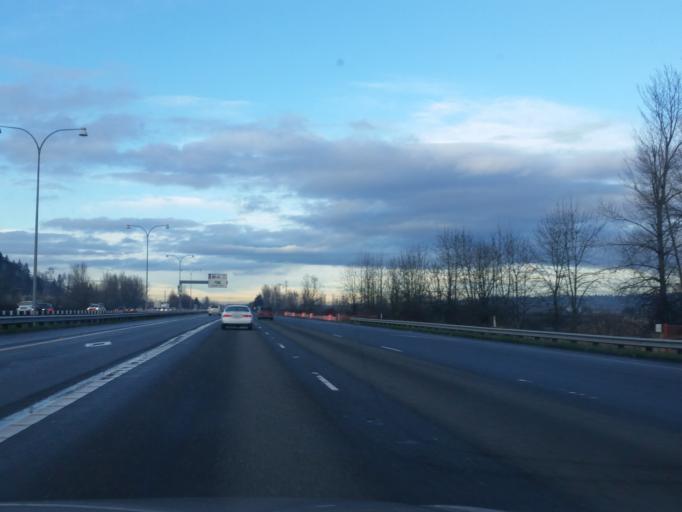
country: US
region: Washington
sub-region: King County
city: Auburn
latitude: 47.3263
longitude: -122.2446
